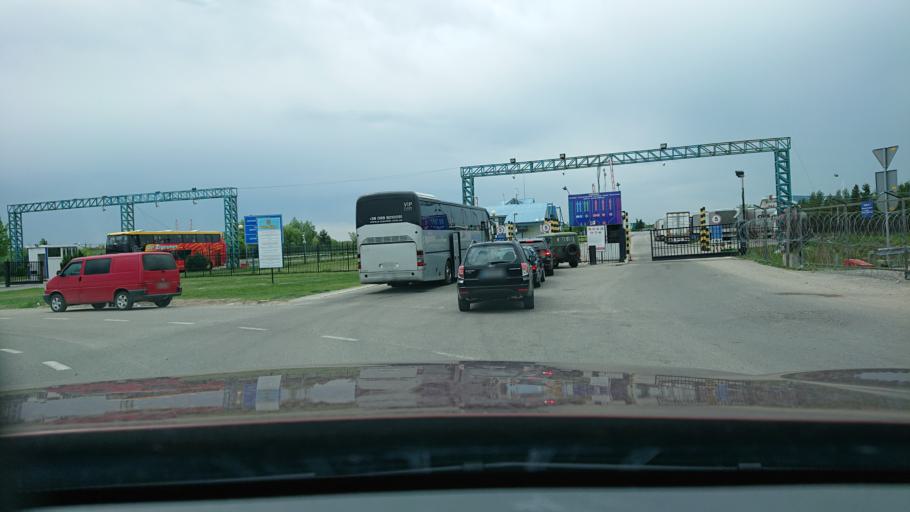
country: PL
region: Subcarpathian Voivodeship
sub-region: Powiat lubaczowski
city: Wielkie Oczy
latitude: 49.9563
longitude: 23.1211
